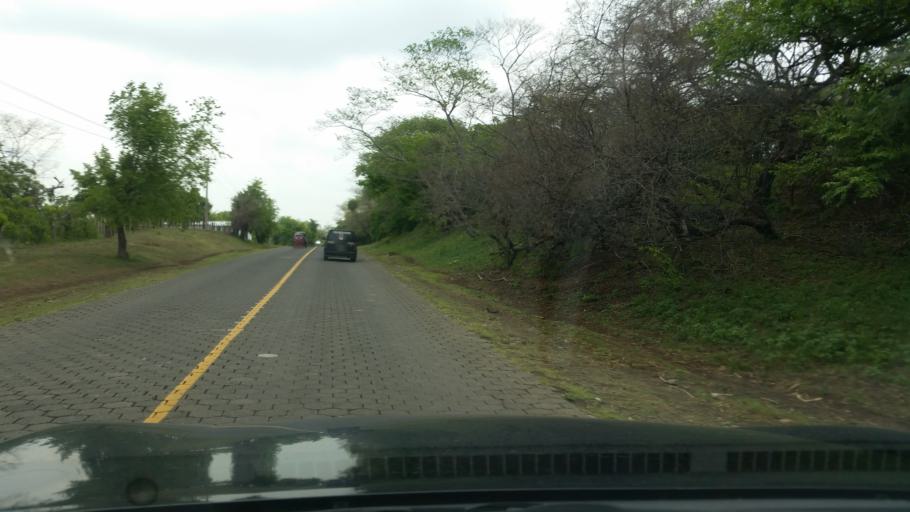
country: NI
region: Managua
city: Masachapa
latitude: 11.8475
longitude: -86.5166
